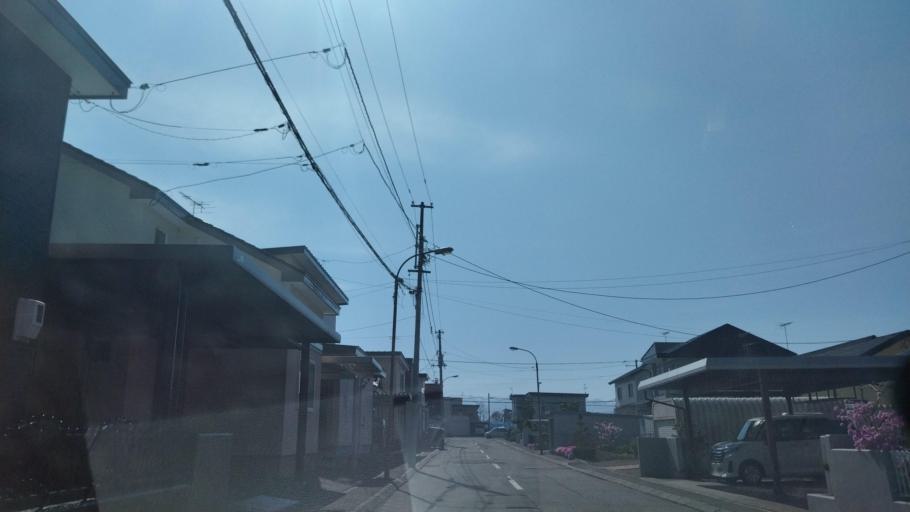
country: JP
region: Hokkaido
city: Obihiro
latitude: 42.9174
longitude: 143.0571
